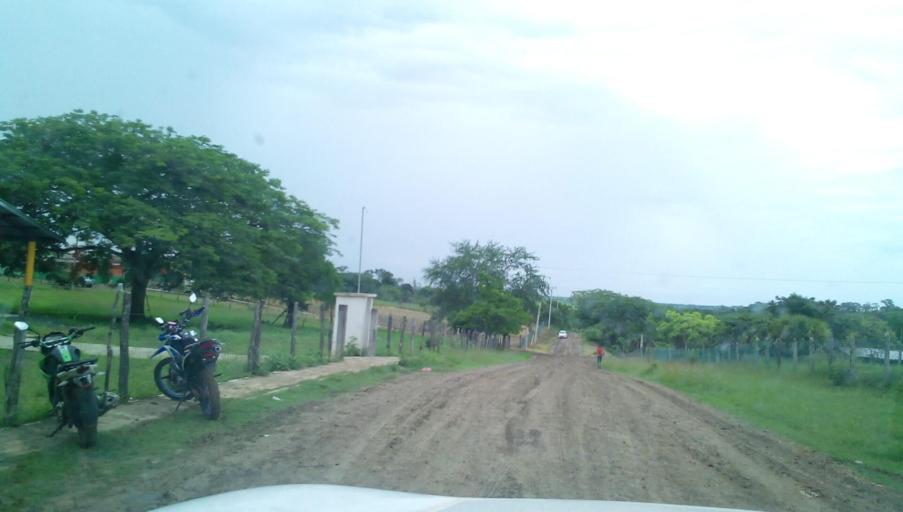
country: MX
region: Veracruz
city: Panuco
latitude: 21.8026
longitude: -98.1065
